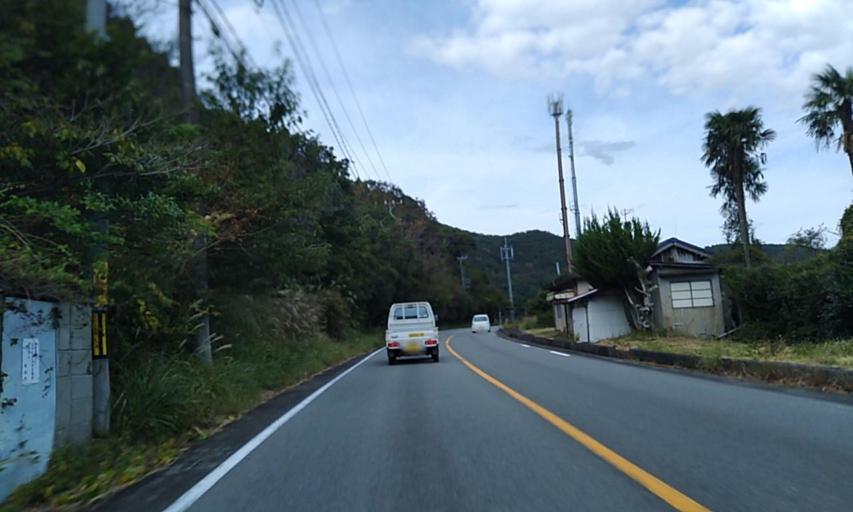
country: JP
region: Mie
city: Ise
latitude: 34.3089
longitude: 136.6364
